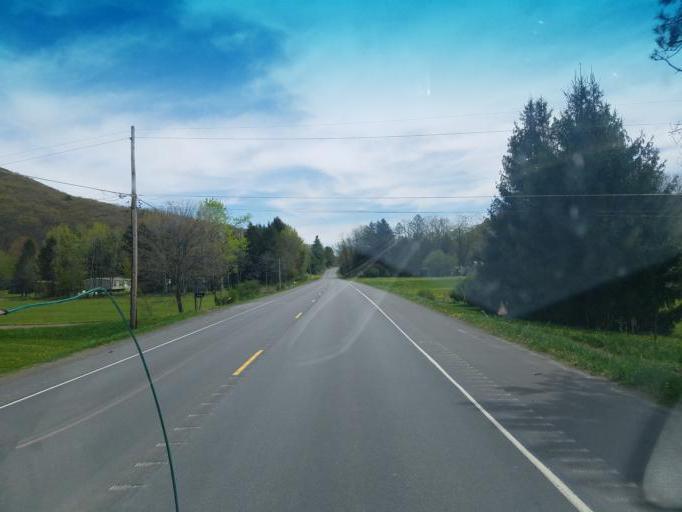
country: US
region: Pennsylvania
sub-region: Potter County
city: Galeton
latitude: 41.7461
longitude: -77.5908
